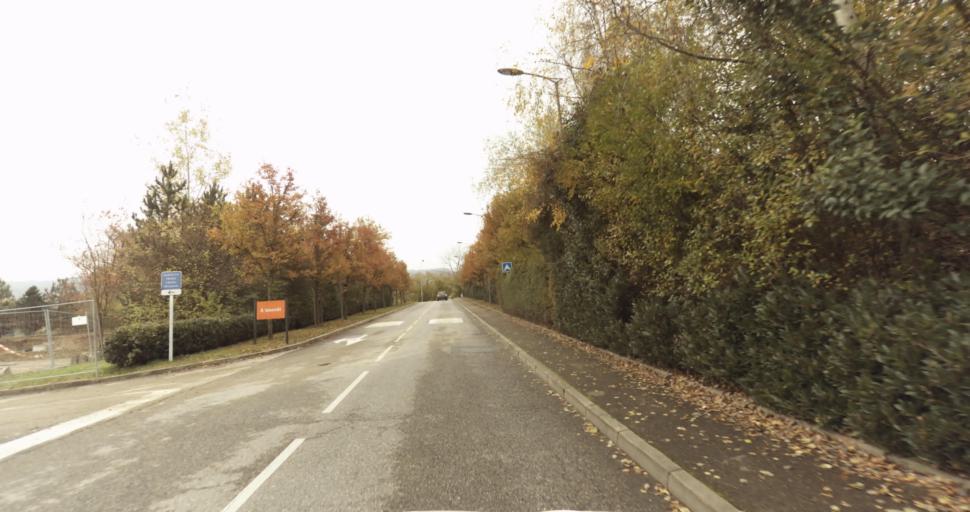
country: FR
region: Rhone-Alpes
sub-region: Departement de la Haute-Savoie
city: Seynod
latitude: 45.8745
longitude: 6.0863
